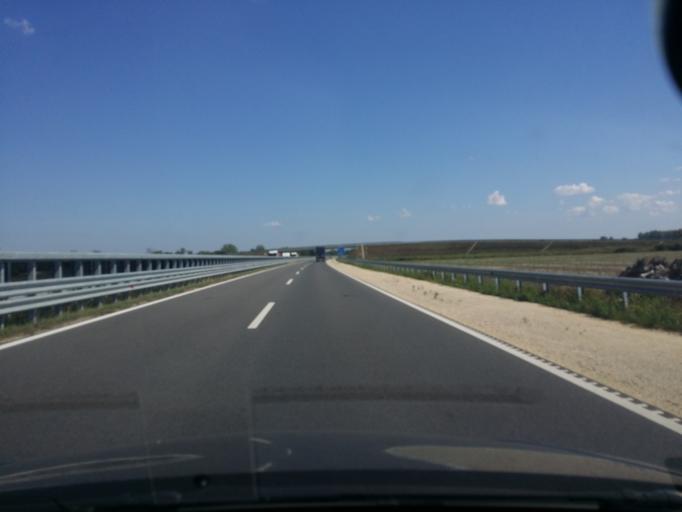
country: HU
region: Gyor-Moson-Sopron
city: Farad
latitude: 47.5428
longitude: 17.2257
